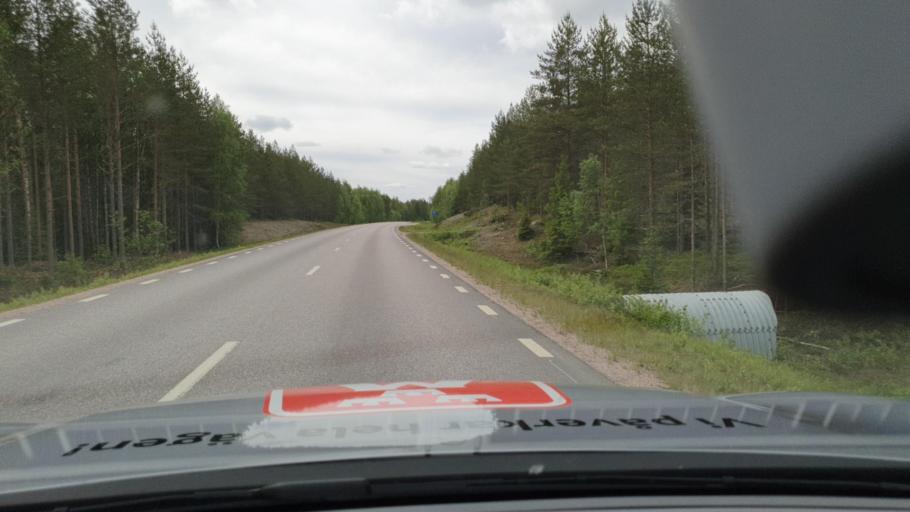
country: SE
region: Norrbotten
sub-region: Kalix Kommun
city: Kalix
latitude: 65.8584
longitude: 23.4785
